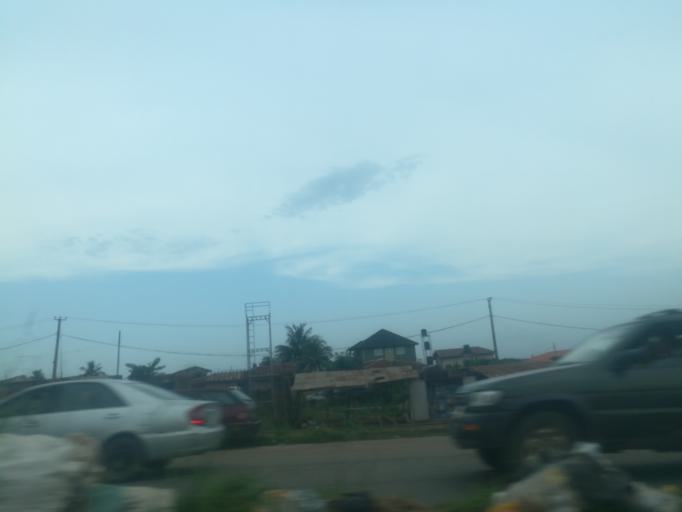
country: NG
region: Oyo
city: Ibadan
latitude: 7.3656
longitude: 3.8158
